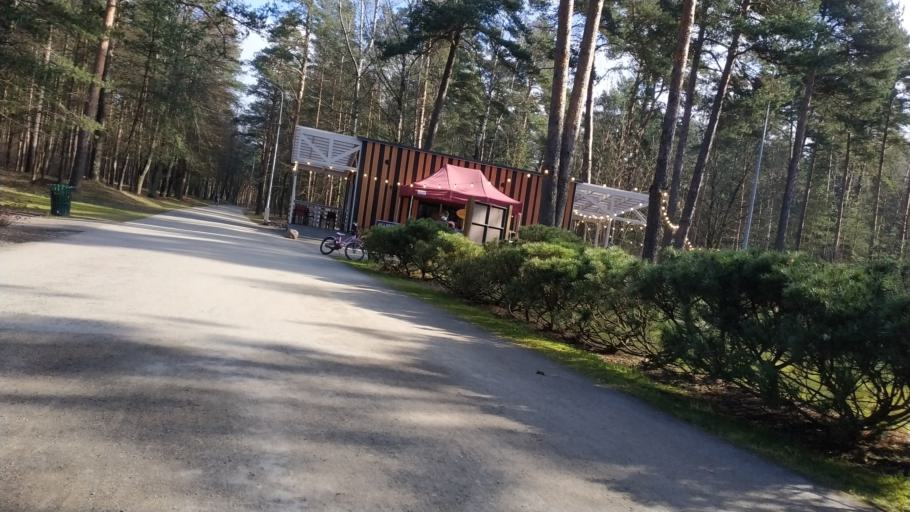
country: LV
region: Riga
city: Jaunciems
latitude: 57.0105
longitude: 24.1500
